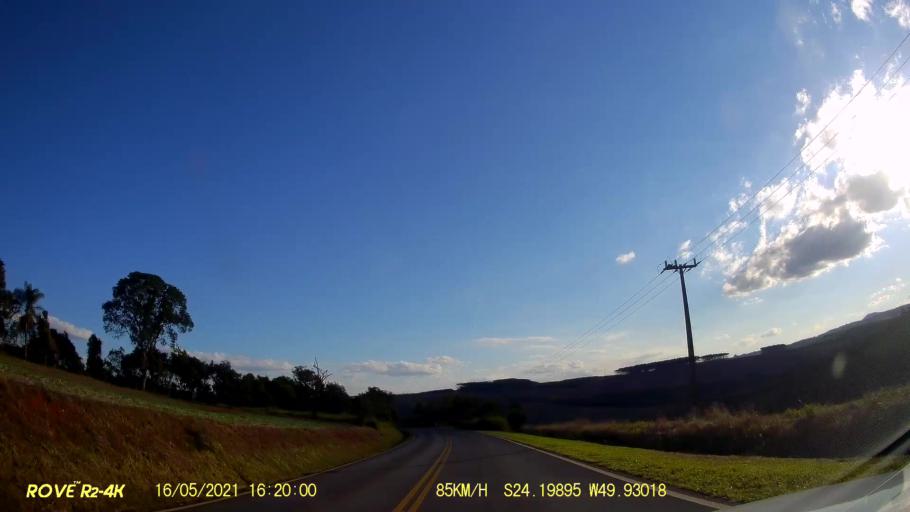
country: BR
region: Parana
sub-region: Jaguariaiva
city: Jaguariaiva
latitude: -24.1992
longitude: -49.9307
